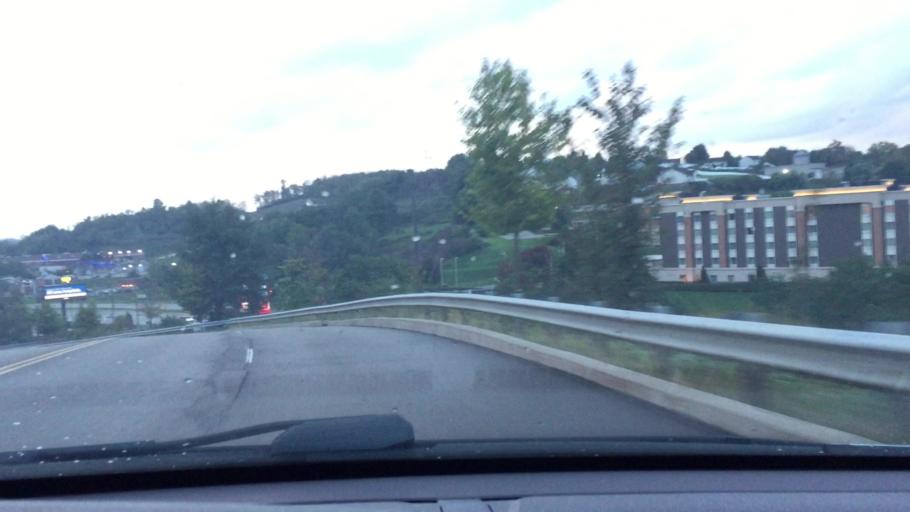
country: US
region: Pennsylvania
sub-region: Washington County
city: McGovern
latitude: 40.2190
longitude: -80.2071
